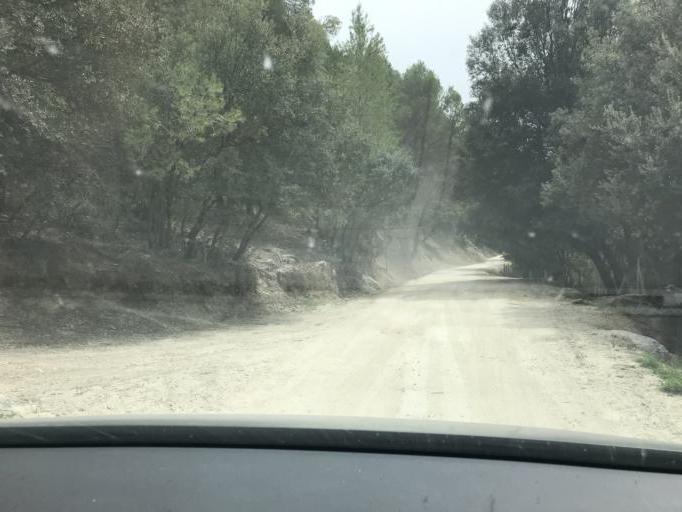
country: ES
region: Andalusia
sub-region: Provincia de Granada
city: Castril
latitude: 37.8444
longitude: -2.7739
